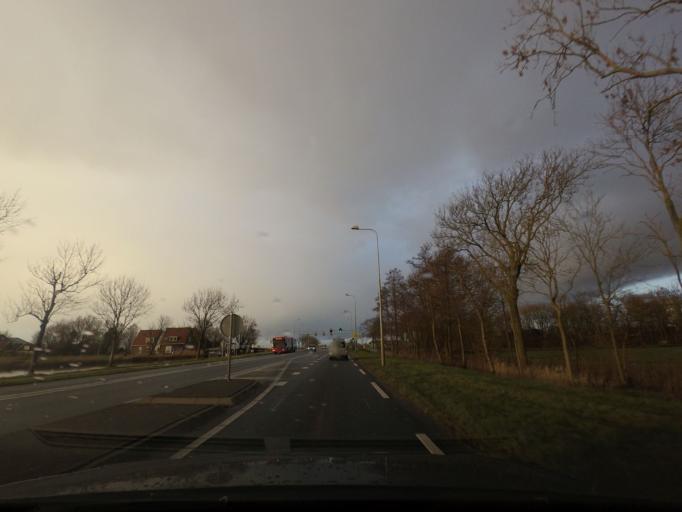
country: NL
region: North Holland
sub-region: Gemeente Waterland
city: Monnickendam
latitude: 52.4817
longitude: 5.0302
